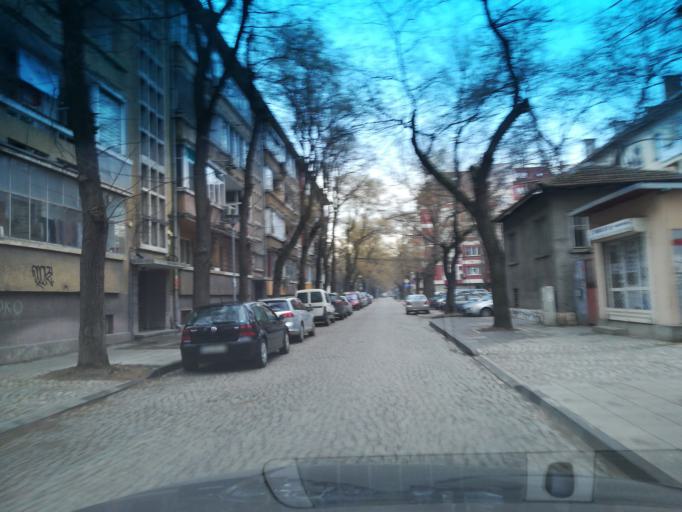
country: BG
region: Plovdiv
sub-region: Obshtina Plovdiv
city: Plovdiv
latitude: 42.1395
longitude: 24.7596
